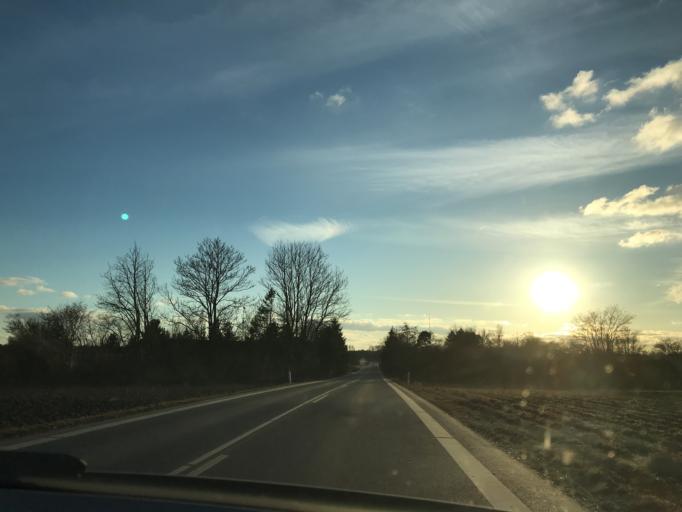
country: DK
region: South Denmark
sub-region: Middelfart Kommune
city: Brenderup
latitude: 55.4700
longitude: 9.9654
